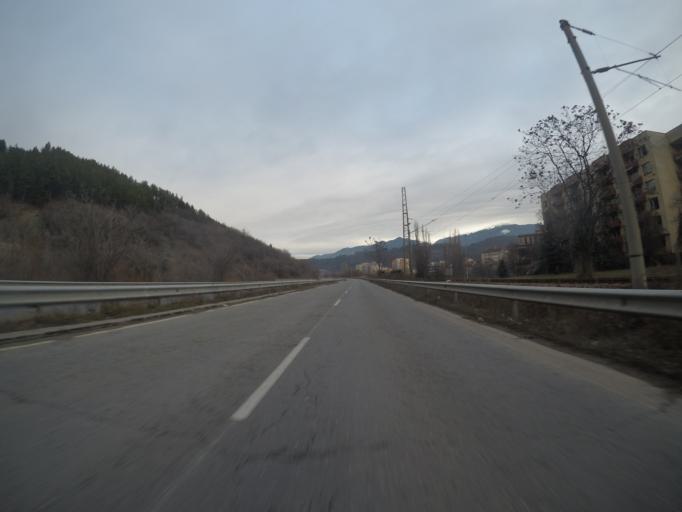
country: BG
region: Kyustendil
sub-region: Obshtina Dupnitsa
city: Dupnitsa
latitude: 42.2681
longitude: 23.1157
